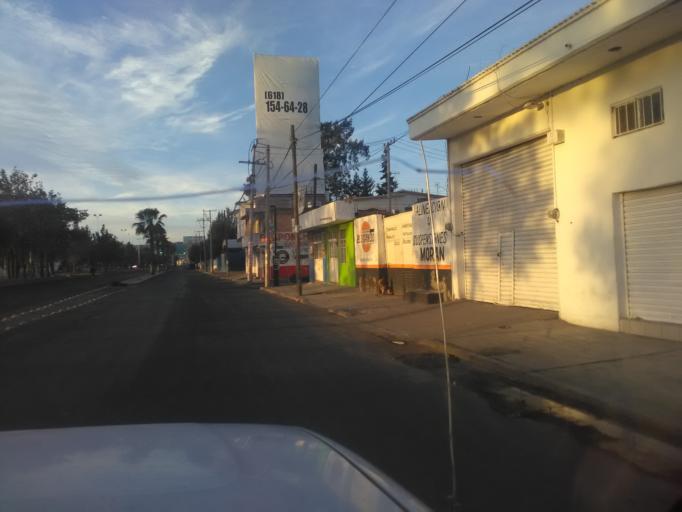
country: MX
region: Durango
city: Victoria de Durango
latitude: 23.9908
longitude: -104.6639
